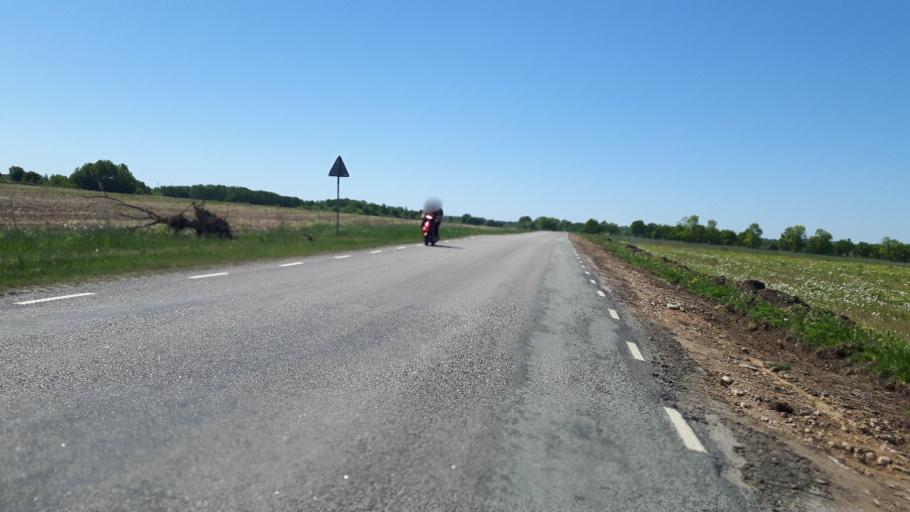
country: EE
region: Ida-Virumaa
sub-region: Narva-Joesuu linn
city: Narva-Joesuu
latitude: 59.4003
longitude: 27.9344
